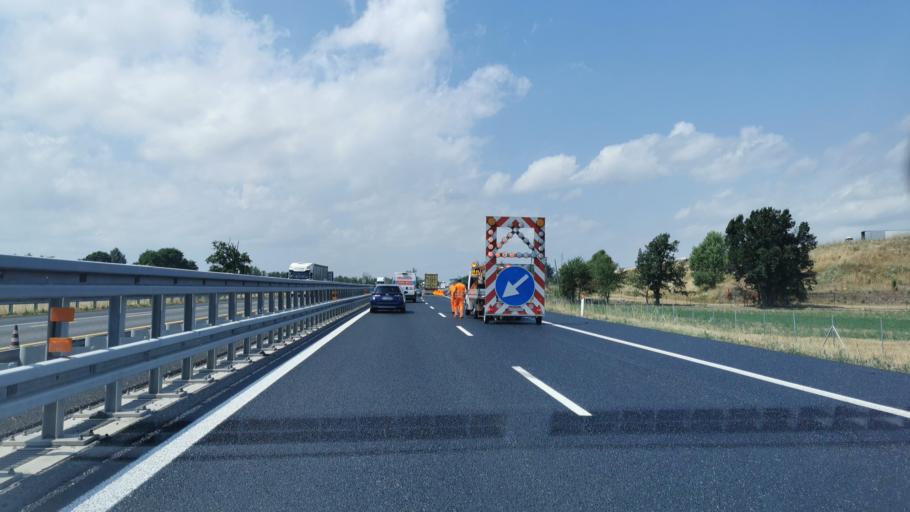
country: IT
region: Piedmont
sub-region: Provincia di Alessandria
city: Tortona
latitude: 44.9204
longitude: 8.8612
